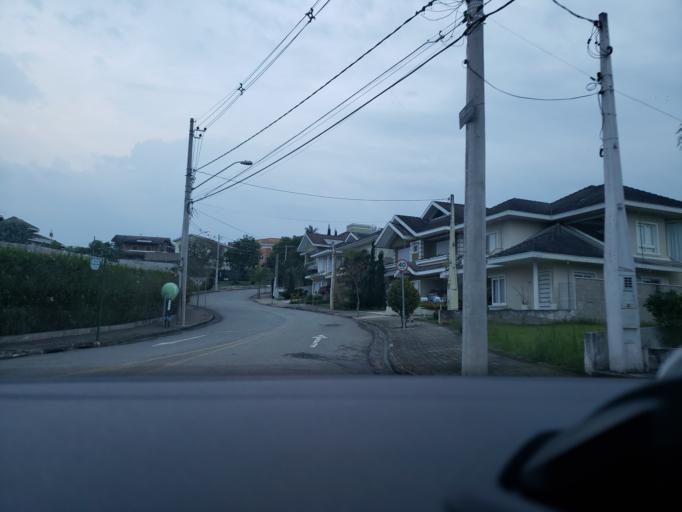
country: BR
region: Sao Paulo
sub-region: Sao Jose Dos Campos
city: Sao Jose dos Campos
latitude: -23.1969
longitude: -45.9482
